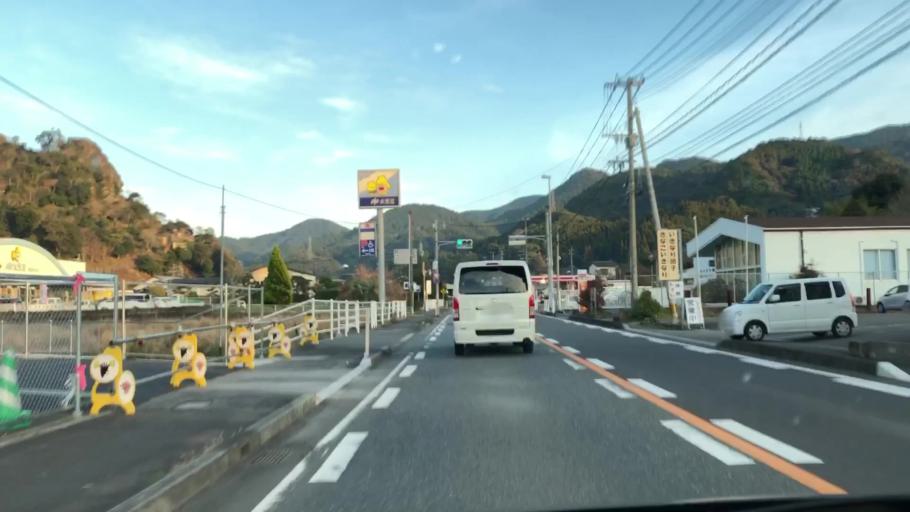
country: JP
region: Kumamoto
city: Minamata
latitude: 32.2325
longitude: 130.4529
